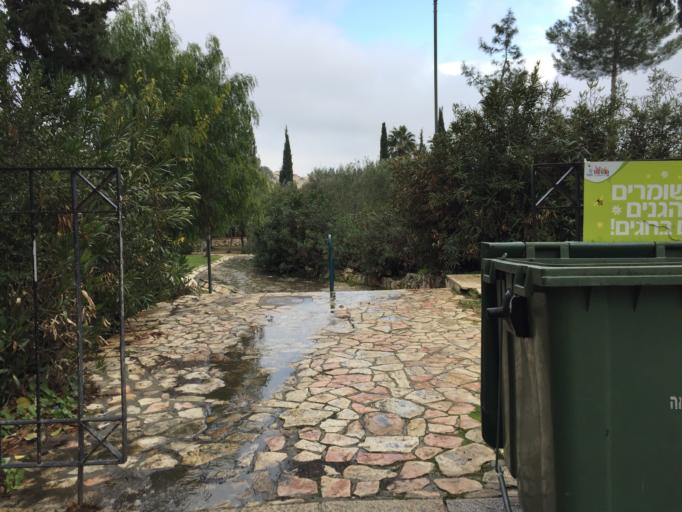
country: IL
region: Jerusalem
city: Jerusalem
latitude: 31.7735
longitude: 35.2233
